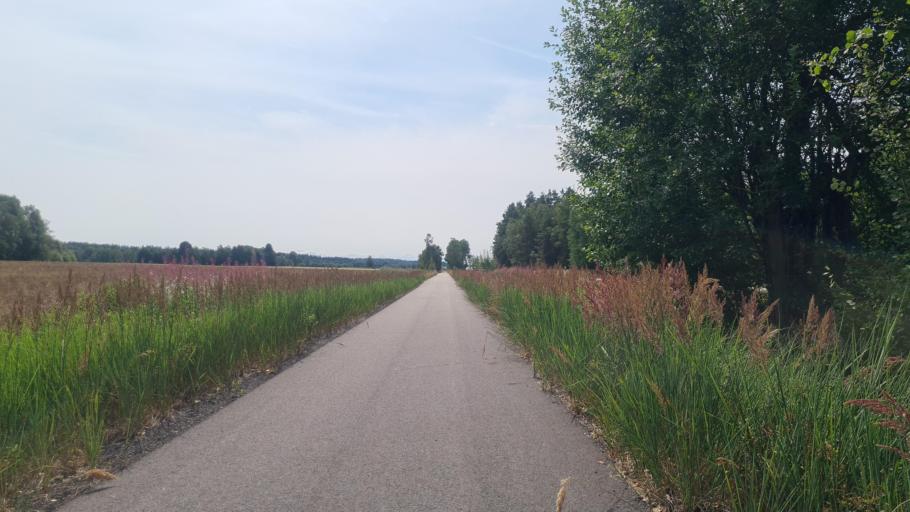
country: SE
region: Kronoberg
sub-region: Ljungby Kommun
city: Lagan
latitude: 56.8886
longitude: 13.9846
